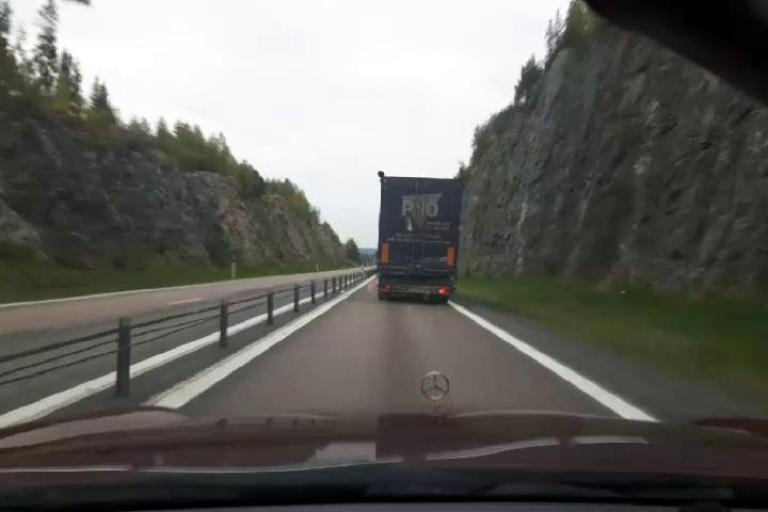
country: SE
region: Vaesternorrland
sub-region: Haernoesands Kommun
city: Haernoesand
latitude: 62.8284
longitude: 17.9682
